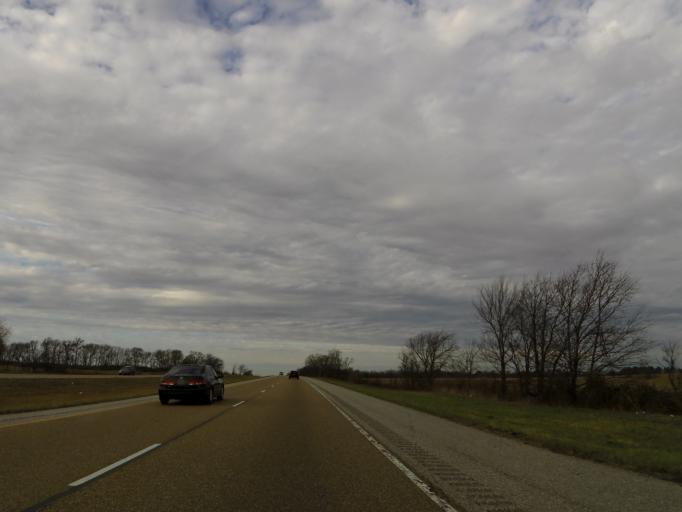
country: US
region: Illinois
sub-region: Clinton County
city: Wamac
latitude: 38.3897
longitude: -89.2241
